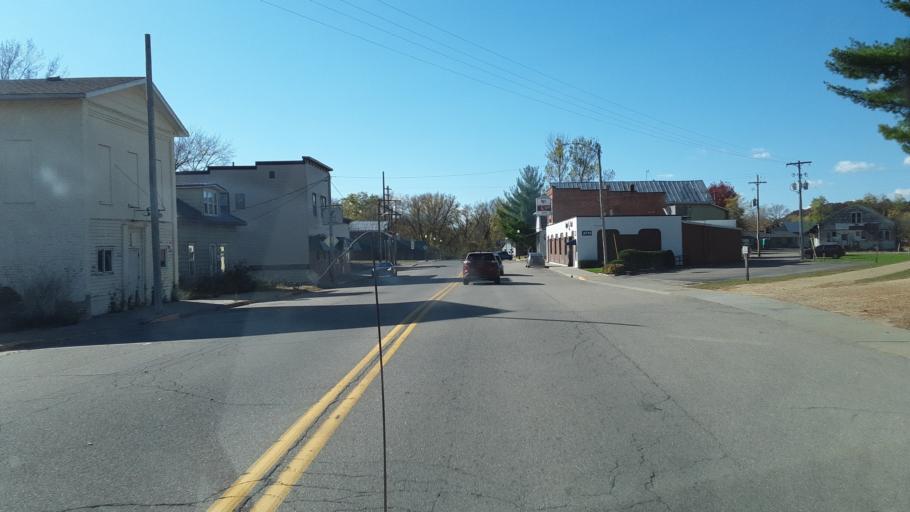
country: US
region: Wisconsin
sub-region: Sauk County
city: Reedsburg
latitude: 43.5825
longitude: -90.1318
